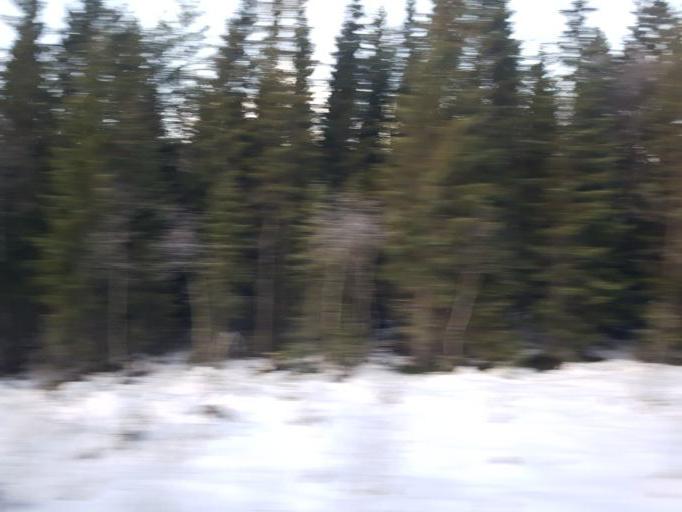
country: NO
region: Sor-Trondelag
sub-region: Rennebu
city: Berkak
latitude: 62.8459
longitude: 10.0182
